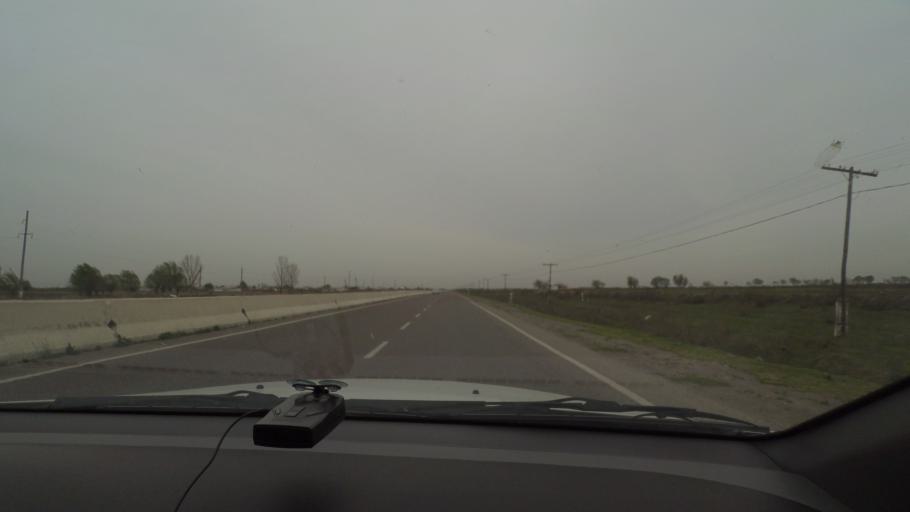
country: UZ
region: Sirdaryo
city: Guliston
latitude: 40.4937
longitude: 68.6667
